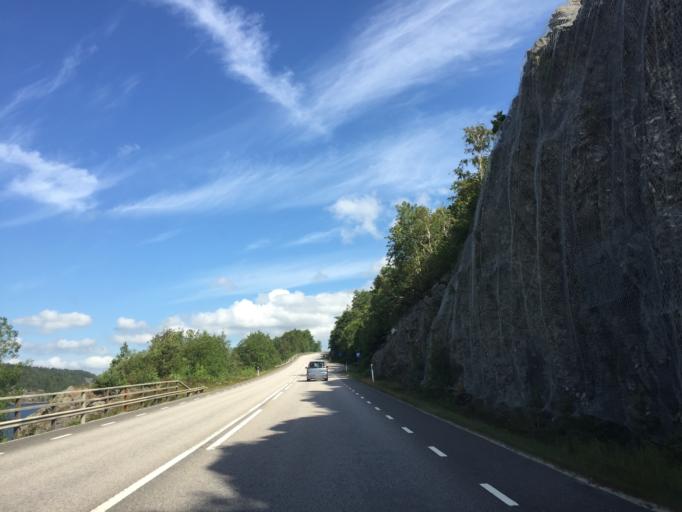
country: SE
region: Vaestra Goetaland
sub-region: Orust
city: Henan
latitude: 58.2566
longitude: 11.6781
